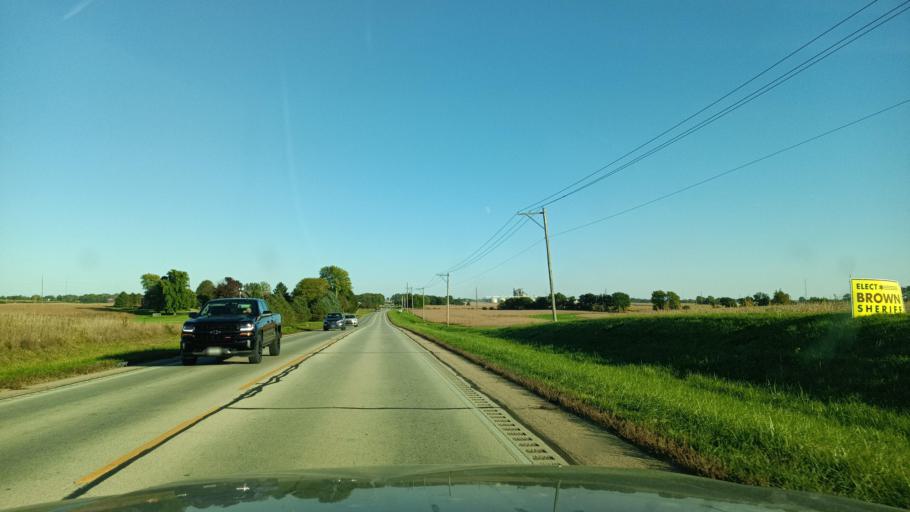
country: US
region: Illinois
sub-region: Champaign County
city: Lake of the Woods
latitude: 40.1748
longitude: -88.3448
